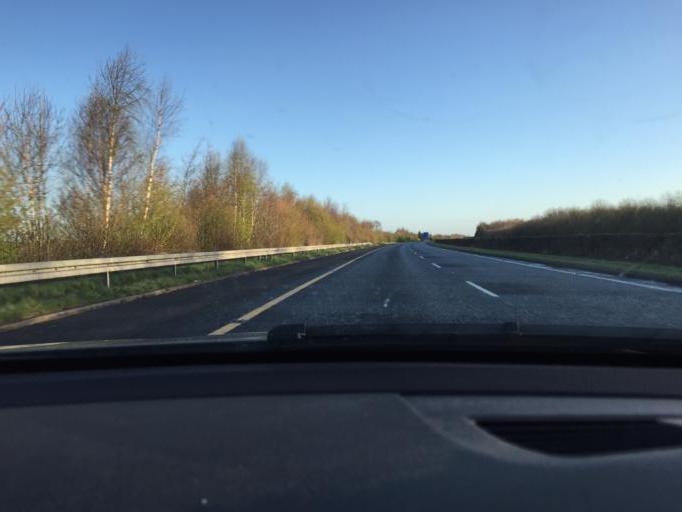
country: IE
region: Leinster
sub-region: Lu
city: Castlebellingham
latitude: 53.8829
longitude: -6.4300
